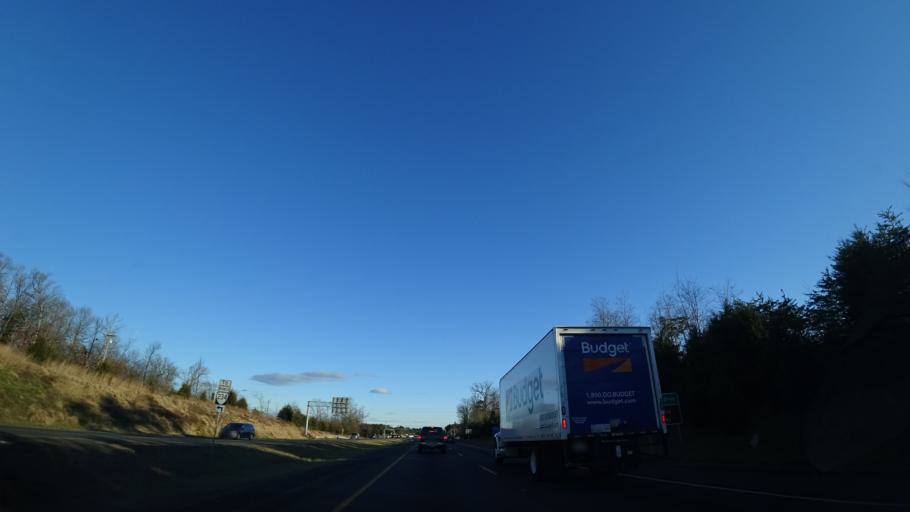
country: US
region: Virginia
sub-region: Prince William County
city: Linton Hall
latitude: 38.7931
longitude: -77.5620
